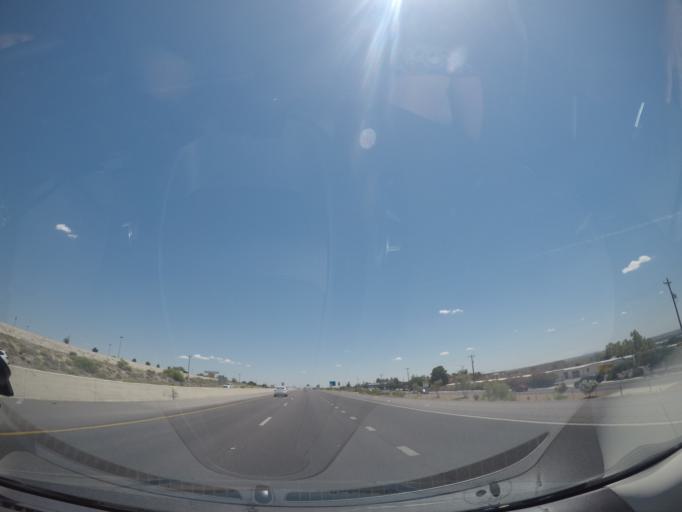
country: US
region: New Mexico
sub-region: Dona Ana County
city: University Park
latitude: 32.3089
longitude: -106.7458
